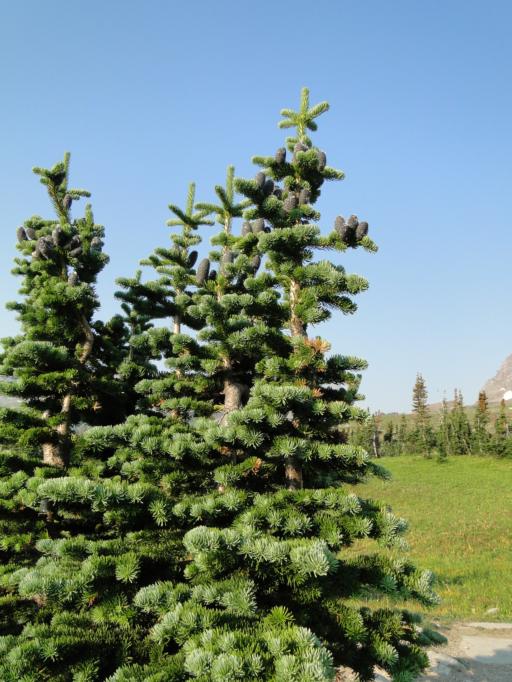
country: US
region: Montana
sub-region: Flathead County
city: Columbia Falls
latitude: 48.6951
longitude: -113.7197
